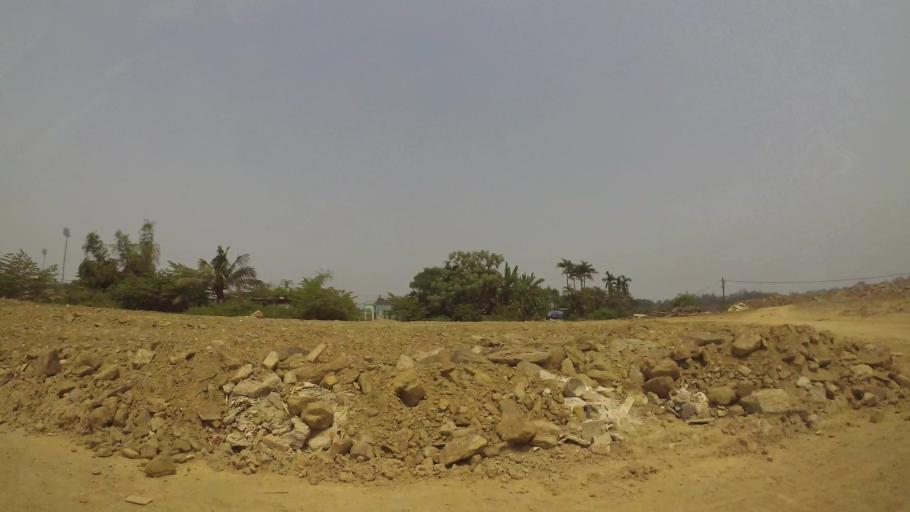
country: VN
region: Da Nang
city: Cam Le
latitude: 15.9960
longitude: 108.2244
